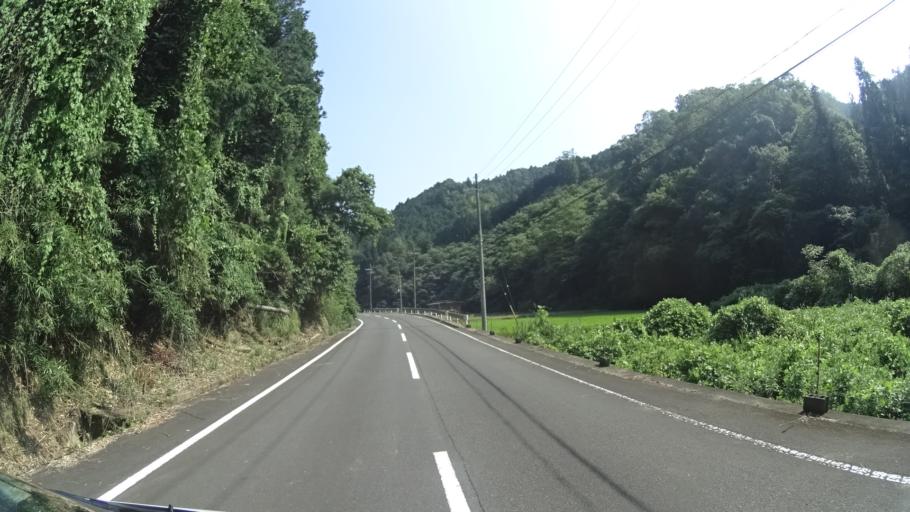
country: JP
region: Kyoto
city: Maizuru
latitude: 35.4190
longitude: 135.2262
